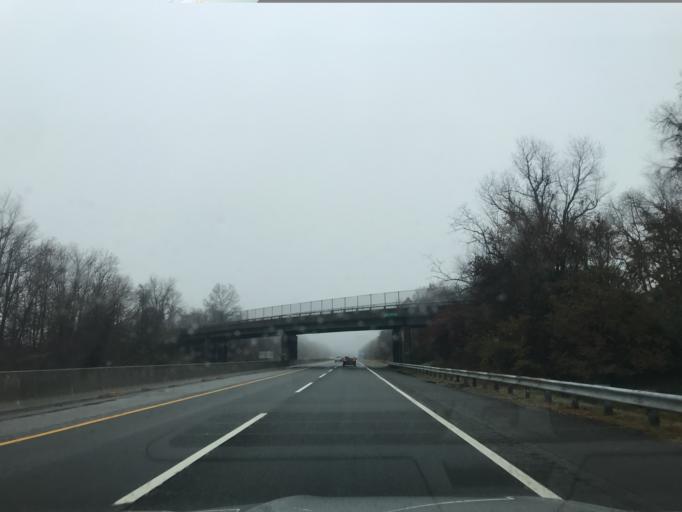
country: US
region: New Jersey
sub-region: Gloucester County
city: Beckett
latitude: 39.7055
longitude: -75.3702
